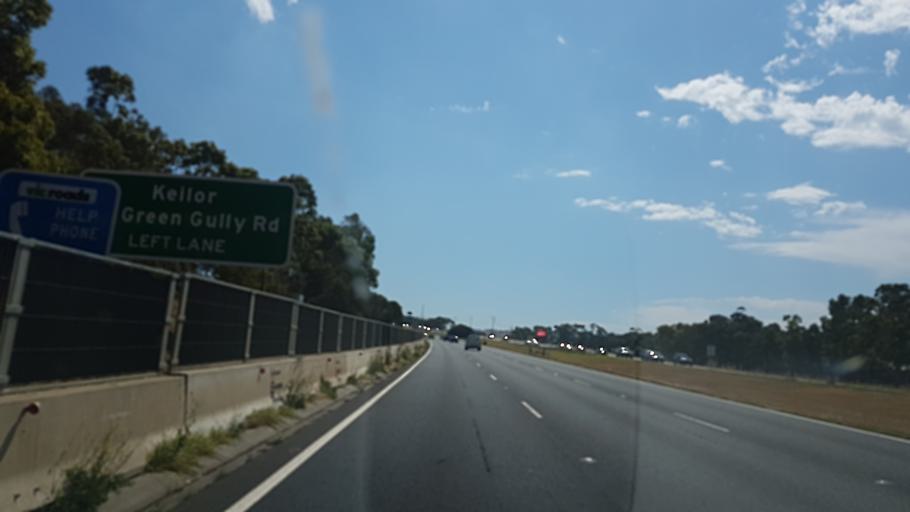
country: AU
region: Victoria
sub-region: Brimbank
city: Keilor
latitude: -37.7168
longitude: 144.8369
